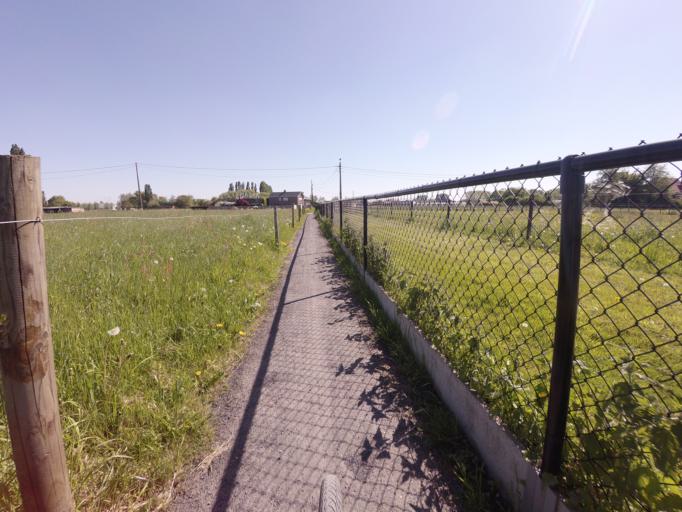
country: BE
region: Flanders
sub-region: Provincie Antwerpen
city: Borsbeek
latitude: 51.1873
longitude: 4.4982
